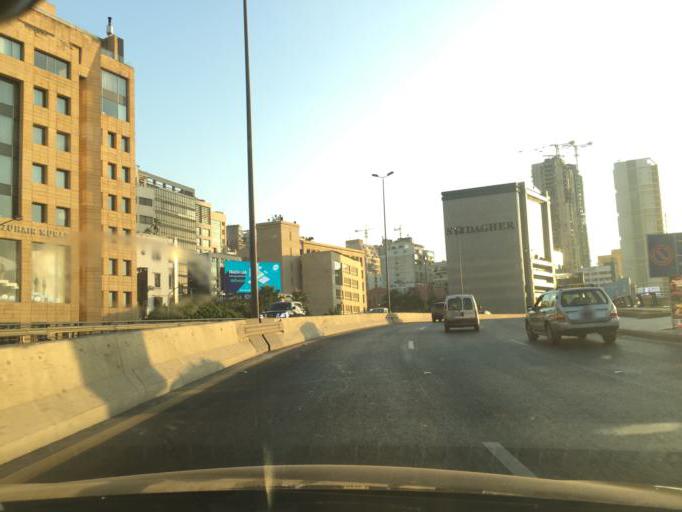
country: LB
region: Beyrouth
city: Beirut
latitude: 33.8966
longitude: 35.5195
